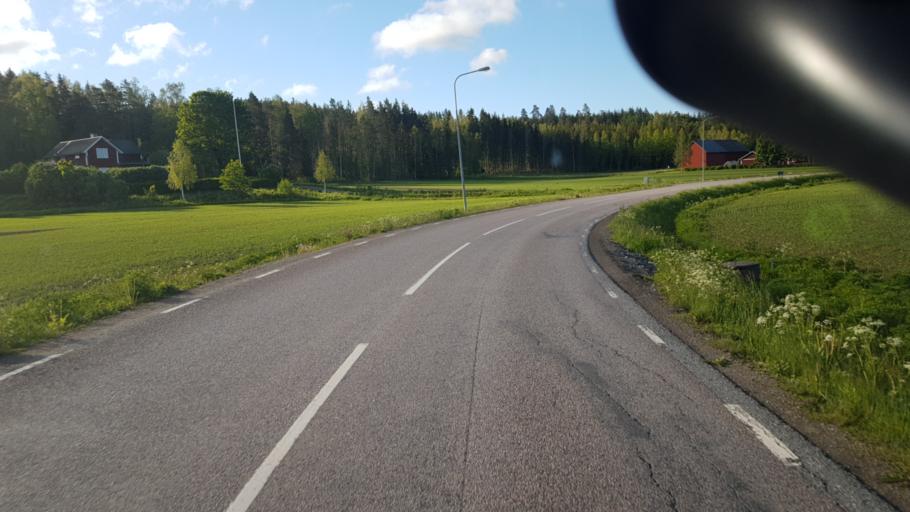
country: SE
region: Vaermland
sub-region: Arvika Kommun
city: Arvika
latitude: 59.5713
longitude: 12.5576
